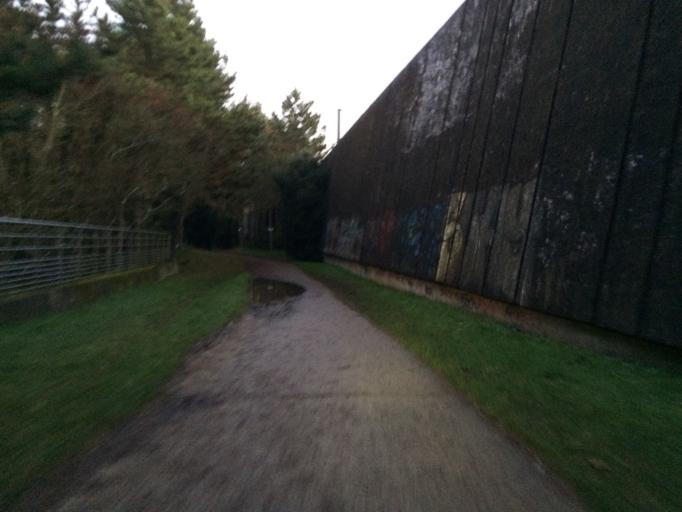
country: FR
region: Ile-de-France
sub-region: Departement de l'Essonne
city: Verrieres-le-Buisson
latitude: 48.7449
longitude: 2.2774
